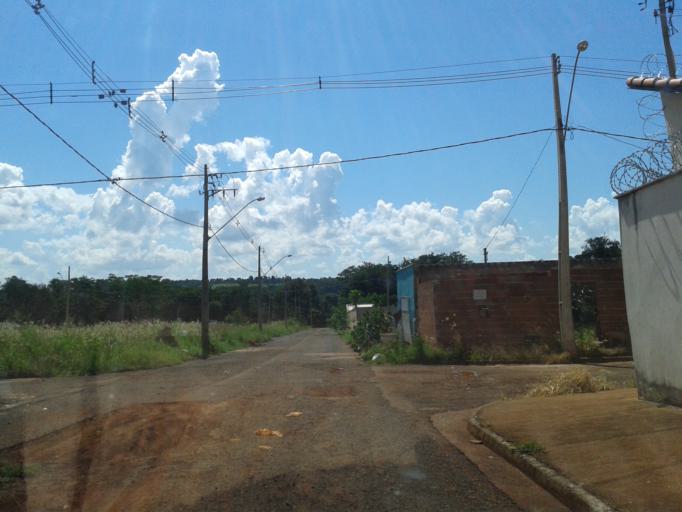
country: BR
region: Goias
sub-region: Itumbiara
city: Itumbiara
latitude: -18.4224
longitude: -49.1851
